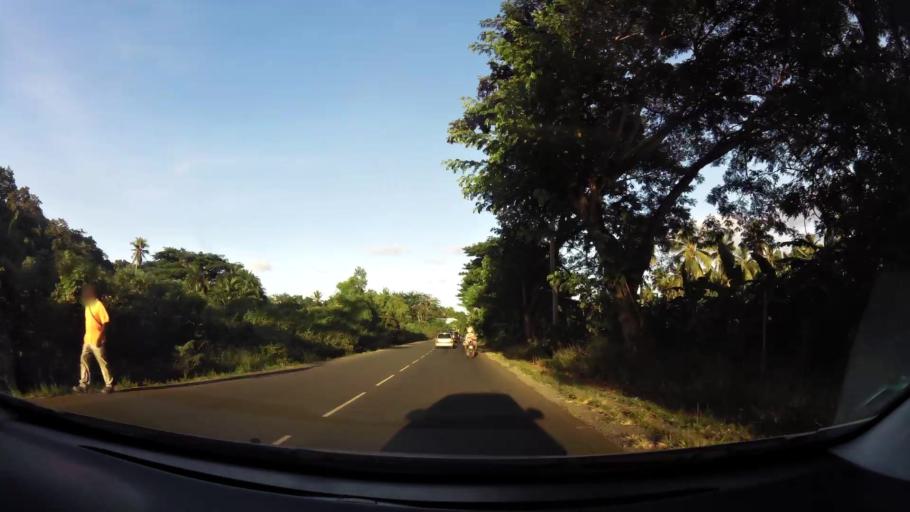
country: YT
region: Dembeni
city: Dembeni
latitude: -12.8390
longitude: 45.1828
